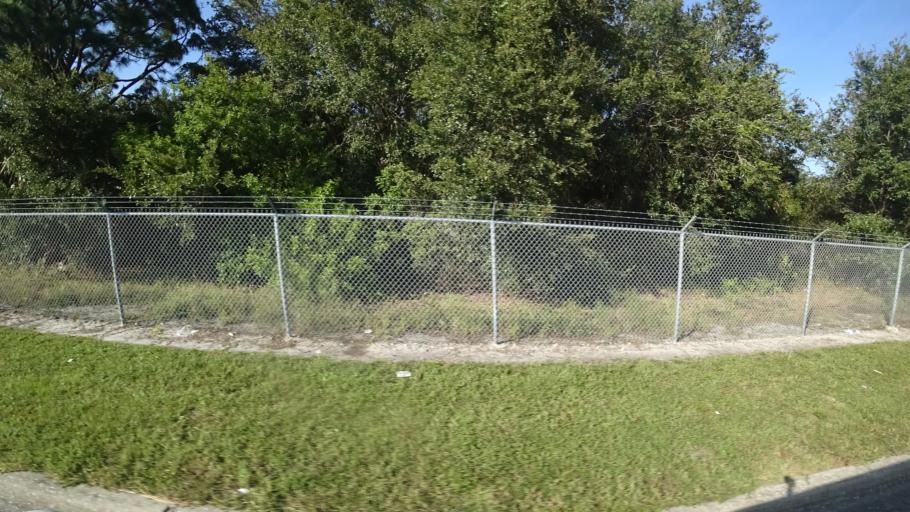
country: US
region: Florida
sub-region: Manatee County
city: Whitfield
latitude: 27.4076
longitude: -82.5659
